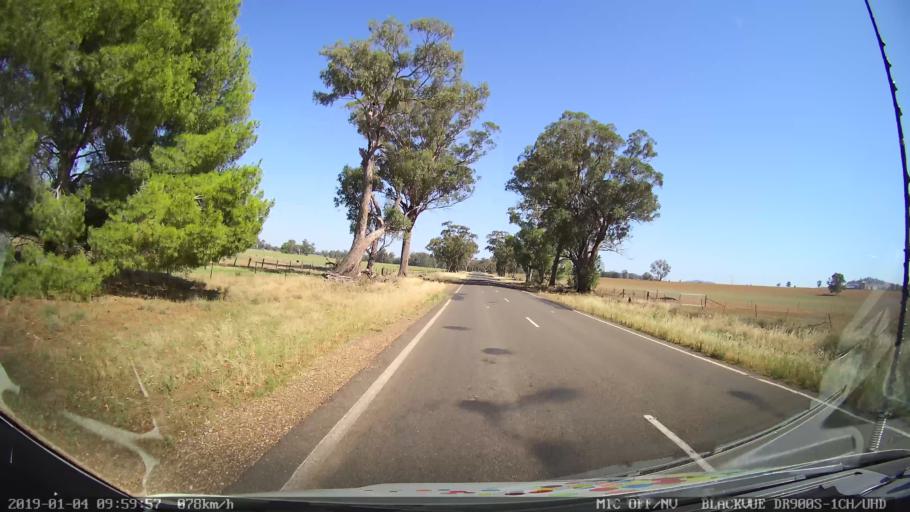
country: AU
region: New South Wales
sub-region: Cabonne
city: Canowindra
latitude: -33.5026
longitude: 148.3825
